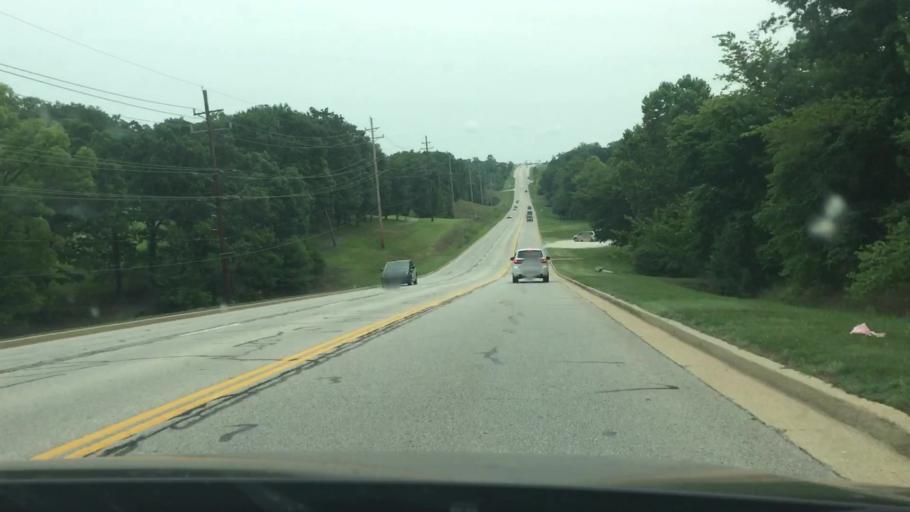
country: US
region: Missouri
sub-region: Miller County
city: Lake Ozark
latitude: 38.1920
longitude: -92.6603
